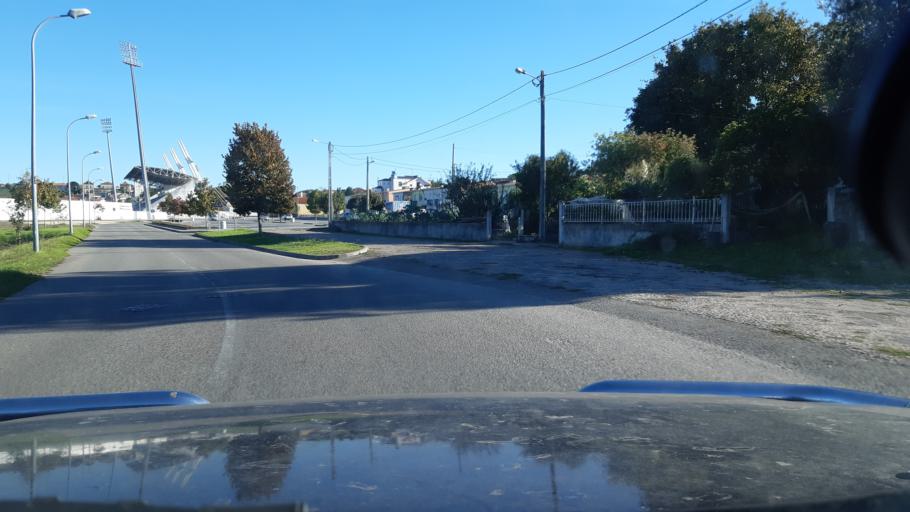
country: PT
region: Aveiro
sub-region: Agueda
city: Agueda
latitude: 40.5639
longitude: -8.4444
